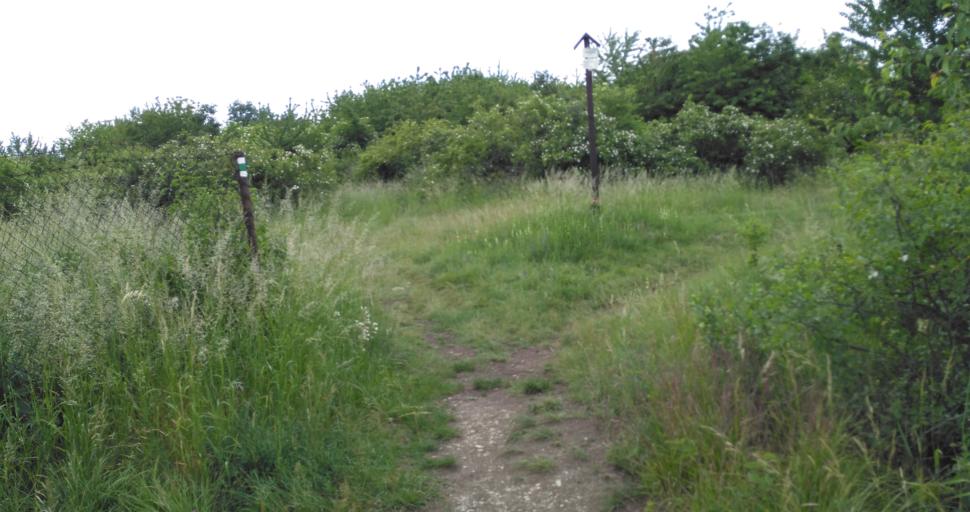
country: CZ
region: South Moravian
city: Podoli
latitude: 49.1895
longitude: 16.6790
